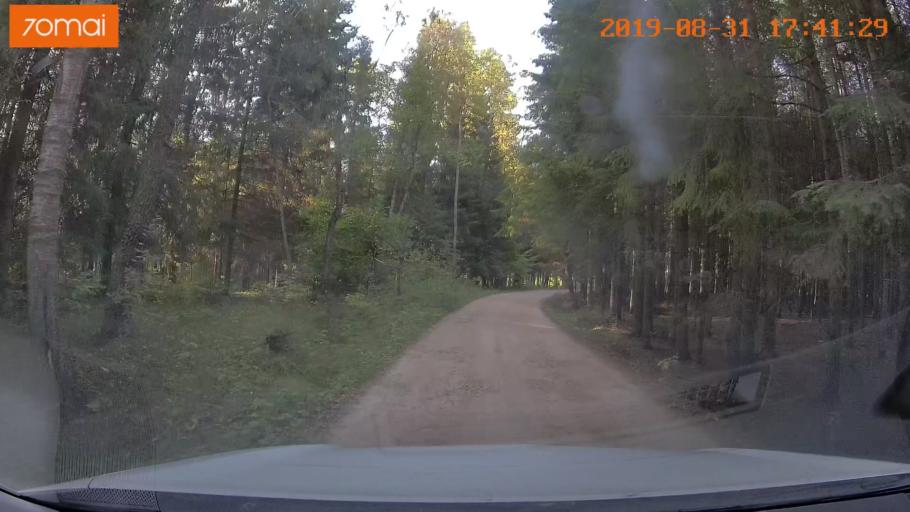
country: RU
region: Kaluga
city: Detchino
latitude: 54.8207
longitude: 36.3655
